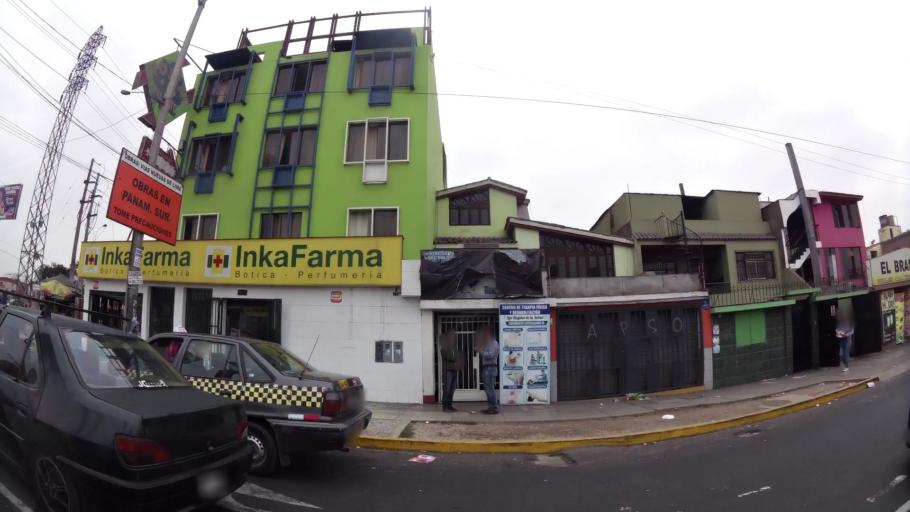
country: PE
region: Lima
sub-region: Lima
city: San Luis
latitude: -12.0780
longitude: -76.9893
